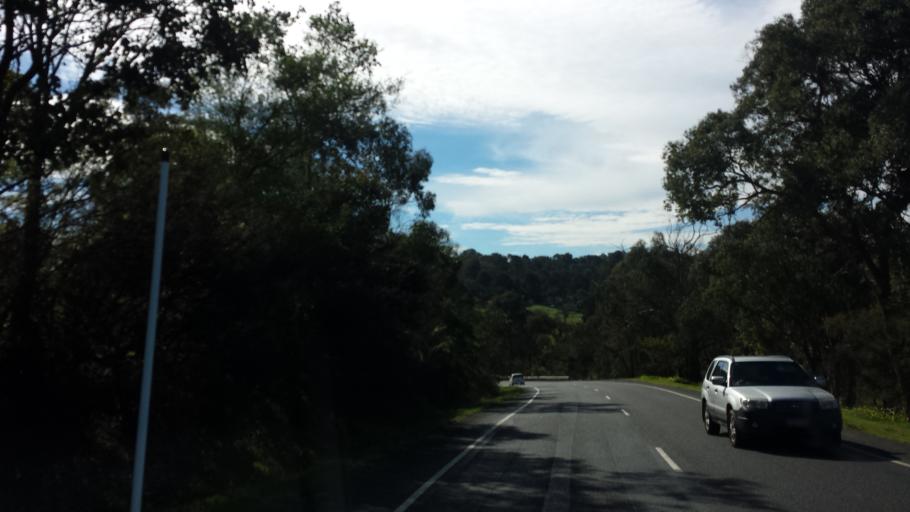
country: AU
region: Victoria
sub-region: Nillumbik
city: Wattleglen
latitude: -37.6792
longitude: 145.2066
